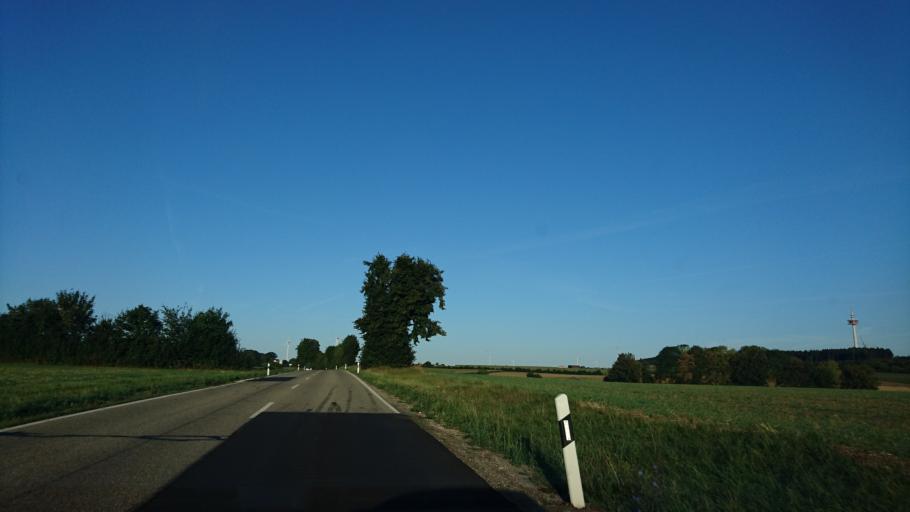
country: DE
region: Bavaria
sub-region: Regierungsbezirk Mittelfranken
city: Burgsalach
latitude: 49.0389
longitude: 11.1091
